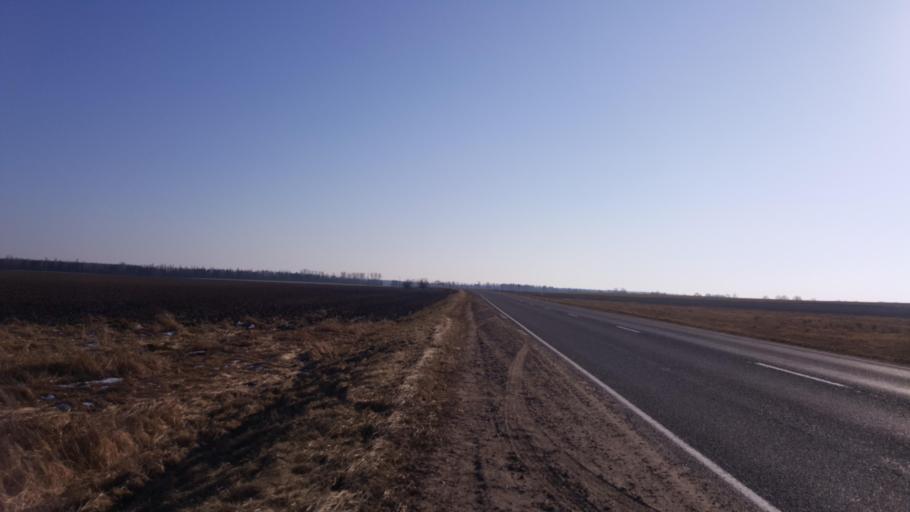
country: BY
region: Brest
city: Kamyanyets
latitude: 52.3849
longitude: 23.7877
